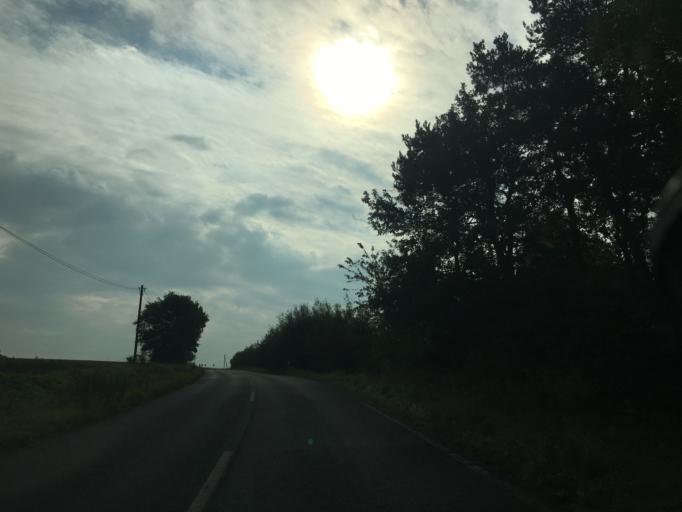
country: DE
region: Hesse
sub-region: Regierungsbezirk Darmstadt
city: Steinau an der Strasse
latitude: 50.2998
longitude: 9.4854
